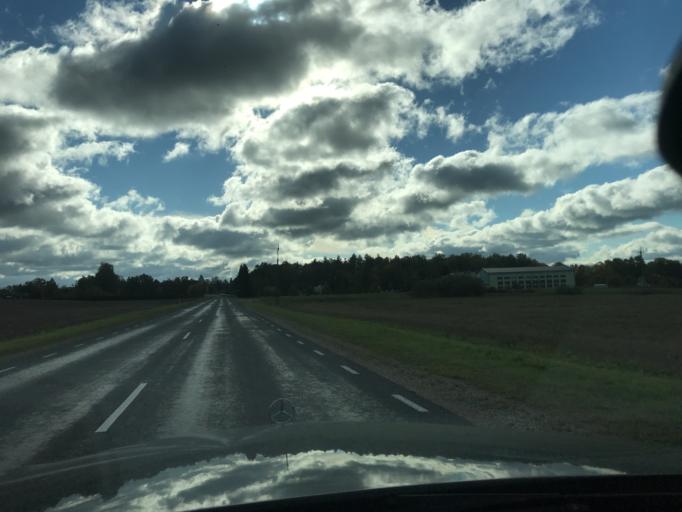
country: EE
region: Vorumaa
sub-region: Antsla vald
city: Vana-Antsla
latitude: 57.9602
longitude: 26.2727
